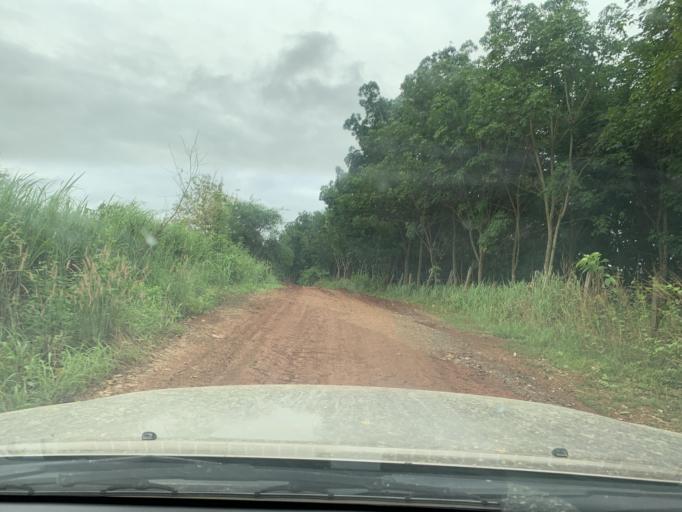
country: TH
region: Nan
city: Mae Charim
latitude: 18.4103
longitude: 101.4410
